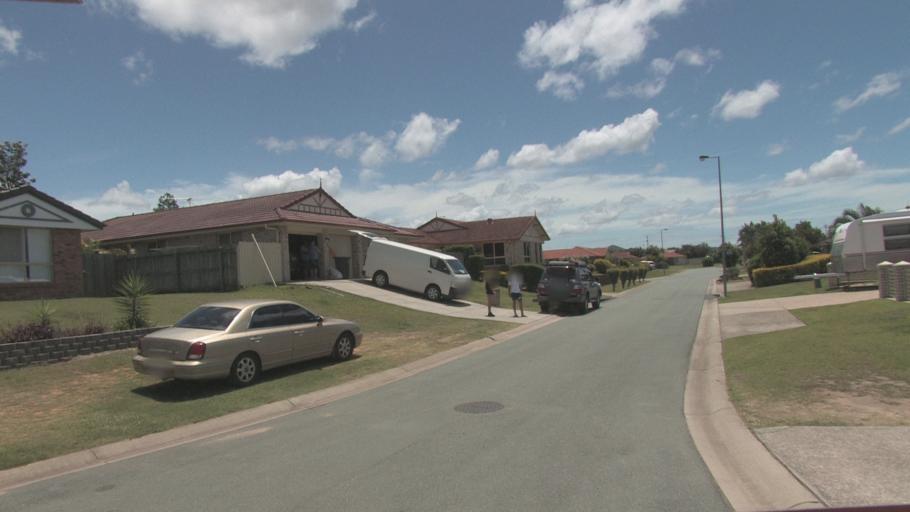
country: AU
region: Queensland
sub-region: Logan
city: Beenleigh
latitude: -27.6966
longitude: 153.2084
